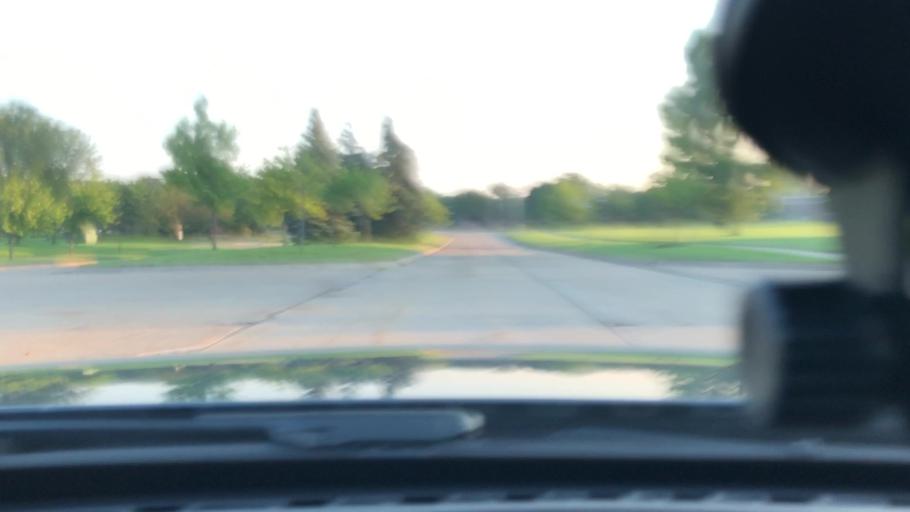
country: US
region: Michigan
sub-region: Wayne County
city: Northville
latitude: 42.3970
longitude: -83.5000
